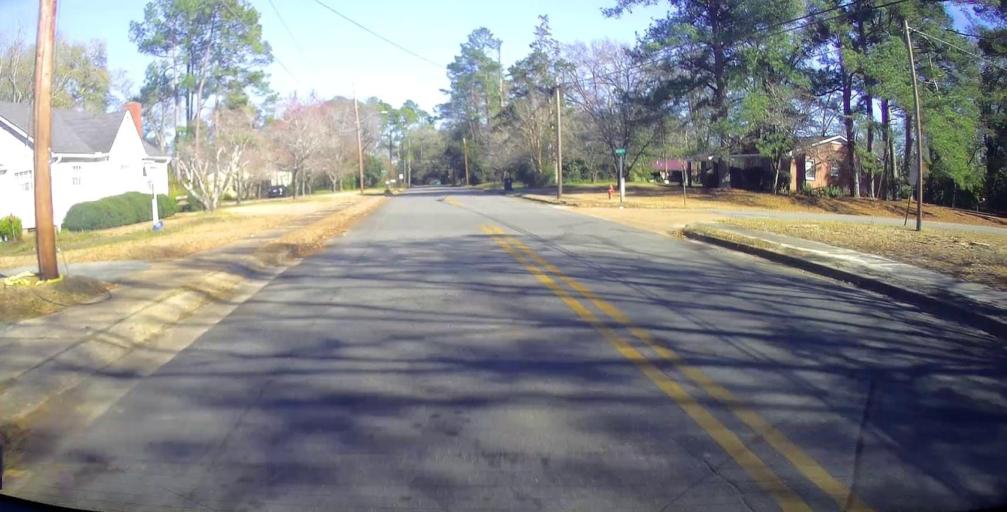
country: US
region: Georgia
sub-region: Macon County
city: Oglethorpe
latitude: 32.3016
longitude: -84.0674
